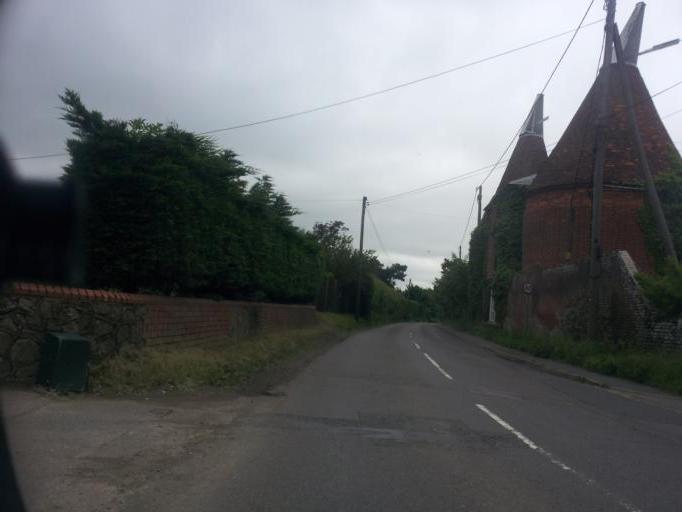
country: GB
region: England
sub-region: Kent
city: Yalding
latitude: 51.2155
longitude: 0.4193
